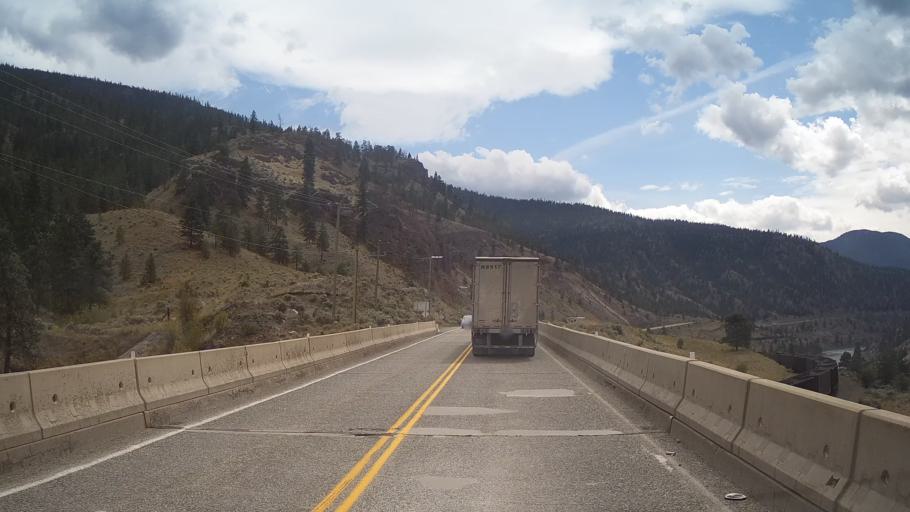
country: CA
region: British Columbia
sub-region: Thompson-Nicola Regional District
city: Ashcroft
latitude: 50.3115
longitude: -121.3958
